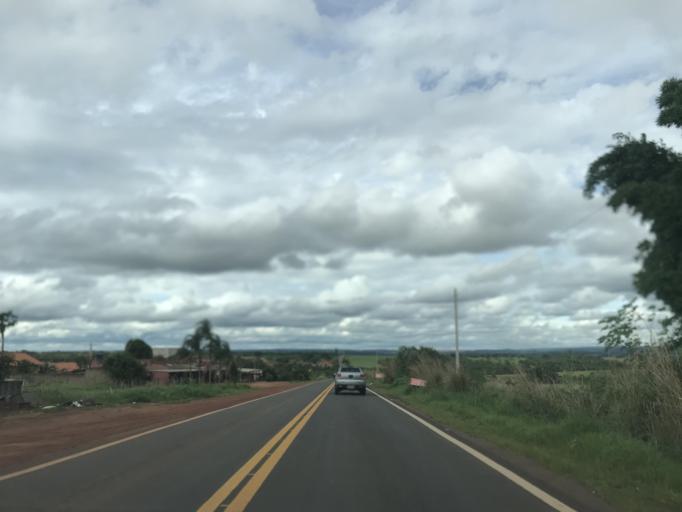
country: BR
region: Goias
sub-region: Piracanjuba
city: Piracanjuba
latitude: -17.2018
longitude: -48.7028
